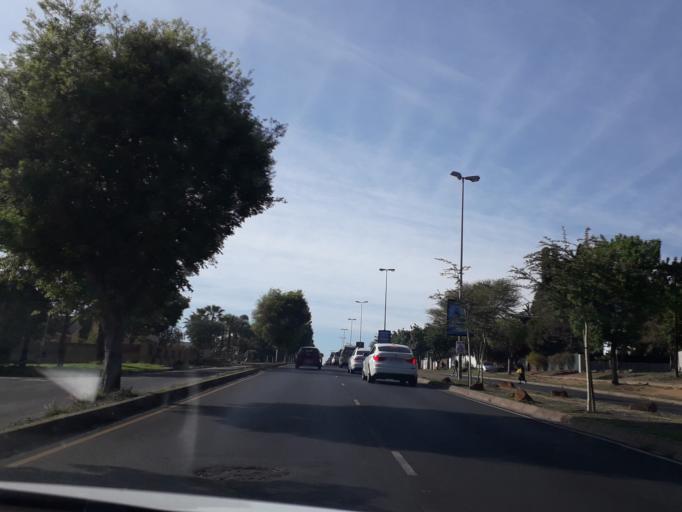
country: ZA
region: Gauteng
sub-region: City of Johannesburg Metropolitan Municipality
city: Johannesburg
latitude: -26.1027
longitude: 28.0132
